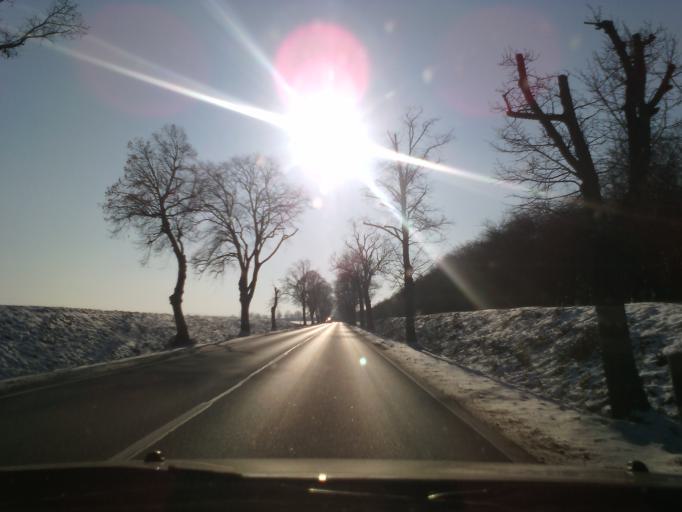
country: PL
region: Lower Silesian Voivodeship
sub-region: Powiat swidnicki
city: Stanowice
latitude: 50.9360
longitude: 16.3637
